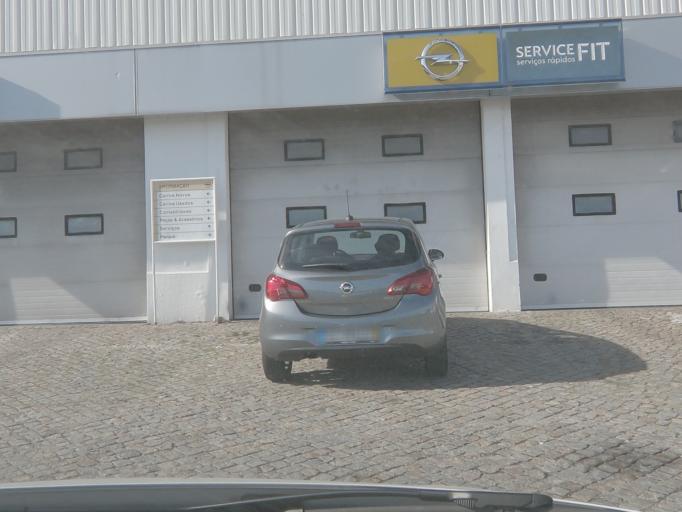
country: PT
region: Viseu
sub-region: Viseu
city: Viseu
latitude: 40.6547
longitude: -7.8959
